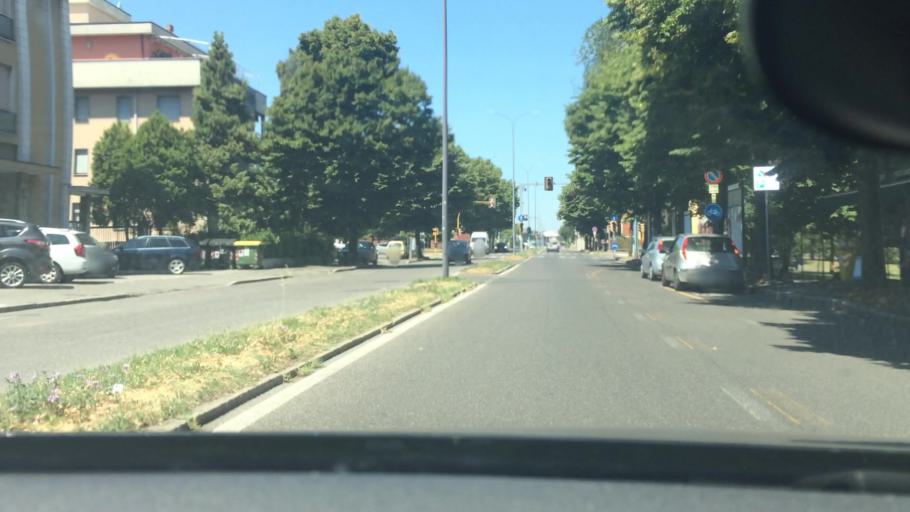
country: IT
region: Emilia-Romagna
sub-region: Provincia di Piacenza
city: Piacenza
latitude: 45.0462
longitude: 9.6700
